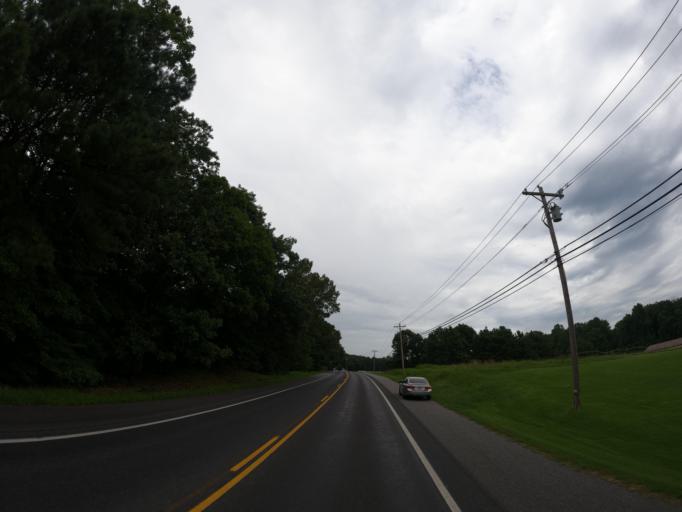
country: US
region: Maryland
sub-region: Saint Mary's County
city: Lexington Park
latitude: 38.2009
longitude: -76.5109
